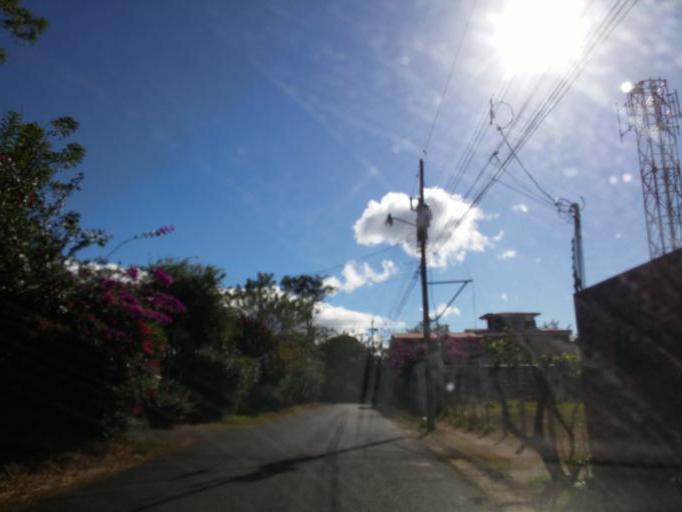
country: CR
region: Alajuela
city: Alajuela
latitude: 10.0278
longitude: -84.2023
